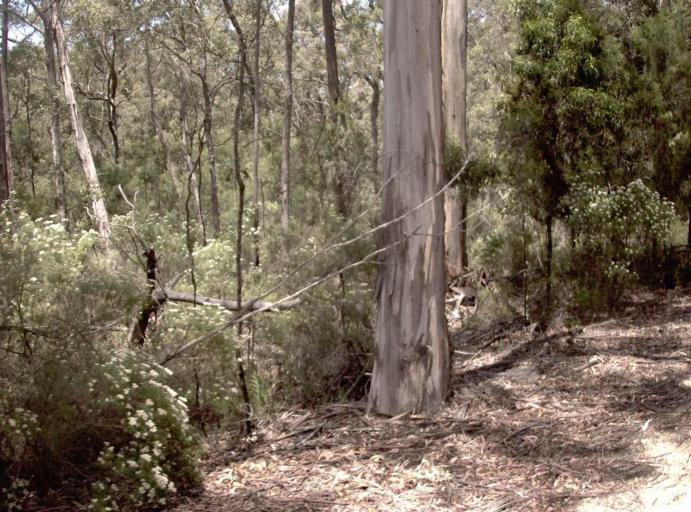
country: AU
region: Victoria
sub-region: East Gippsland
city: Lakes Entrance
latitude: -37.6461
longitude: 147.8941
